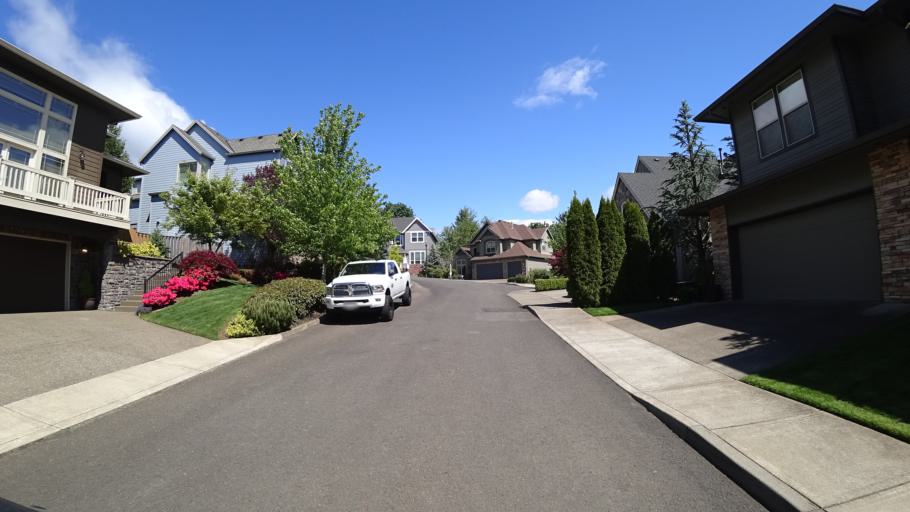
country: US
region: Oregon
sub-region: Washington County
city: West Haven
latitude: 45.5502
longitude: -122.7814
